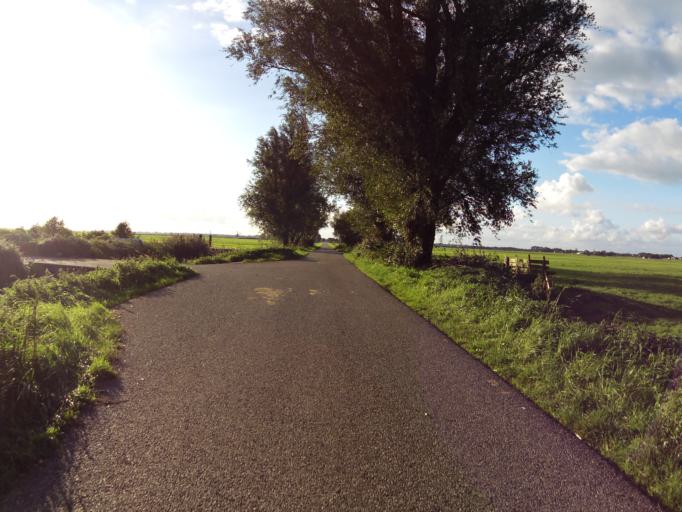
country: NL
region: South Holland
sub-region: Bodegraven-Reeuwijk
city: Bodegraven
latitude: 52.1219
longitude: 4.7488
